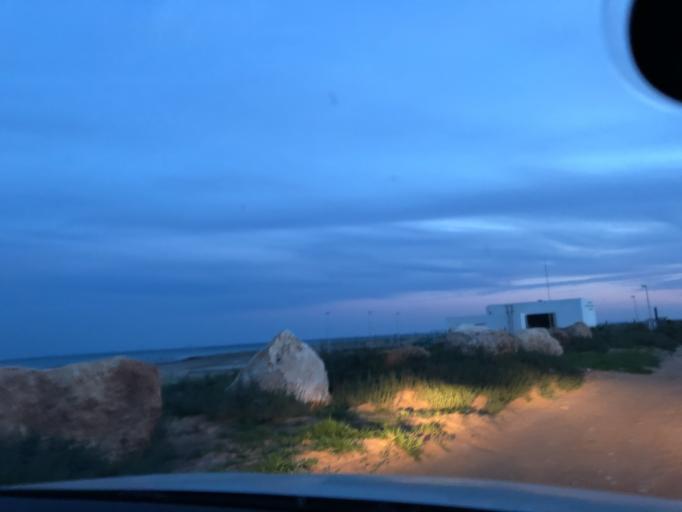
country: CY
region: Larnaka
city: Meneou
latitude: 34.8694
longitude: 33.6379
